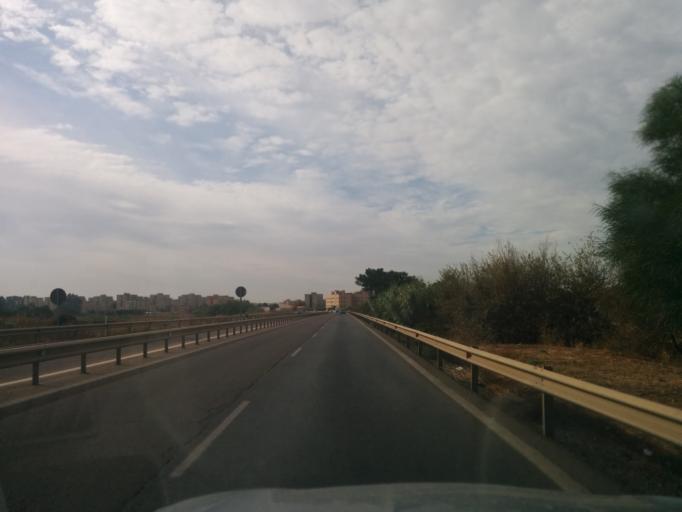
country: ES
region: Andalusia
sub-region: Provincia de Sevilla
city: Sevilla
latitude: 37.4319
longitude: -5.9654
